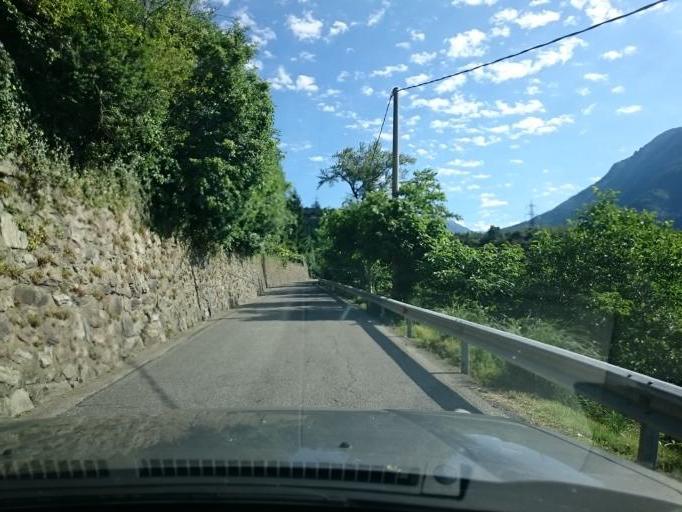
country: IT
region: Lombardy
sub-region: Provincia di Brescia
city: Capo di Ponte
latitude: 46.0309
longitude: 10.3351
